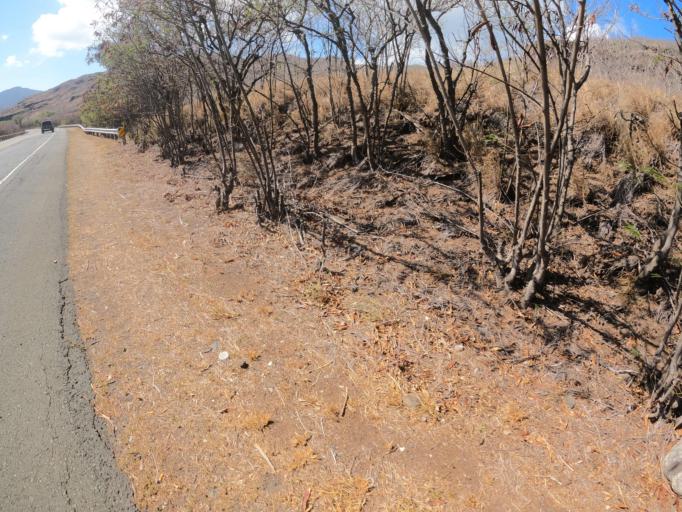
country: US
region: Hawaii
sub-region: Honolulu County
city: Waimanalo Beach
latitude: 21.3012
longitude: -157.6595
